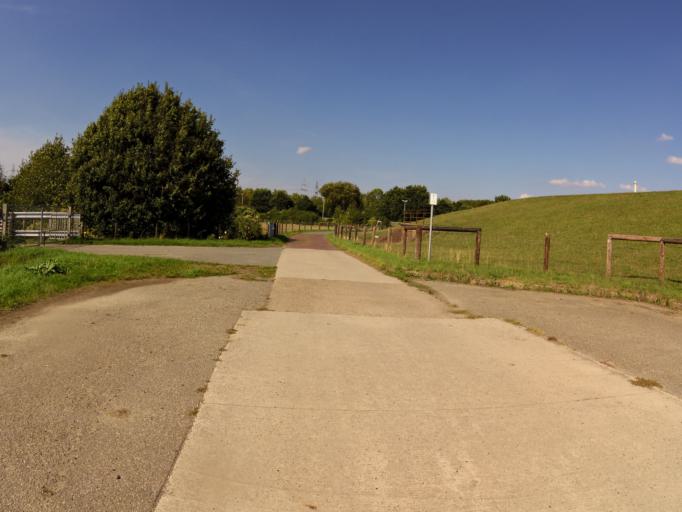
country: DE
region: Lower Saxony
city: Nordenham
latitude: 53.4238
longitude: 8.4717
